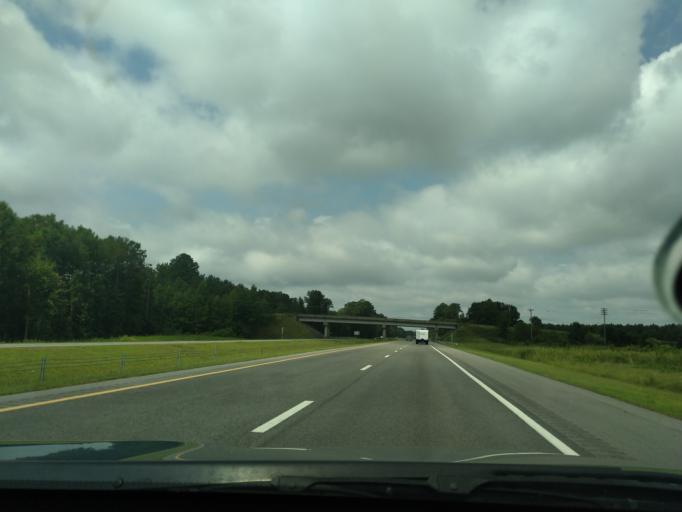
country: US
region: North Carolina
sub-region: Pitt County
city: Bethel
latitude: 35.8334
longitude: -77.3165
